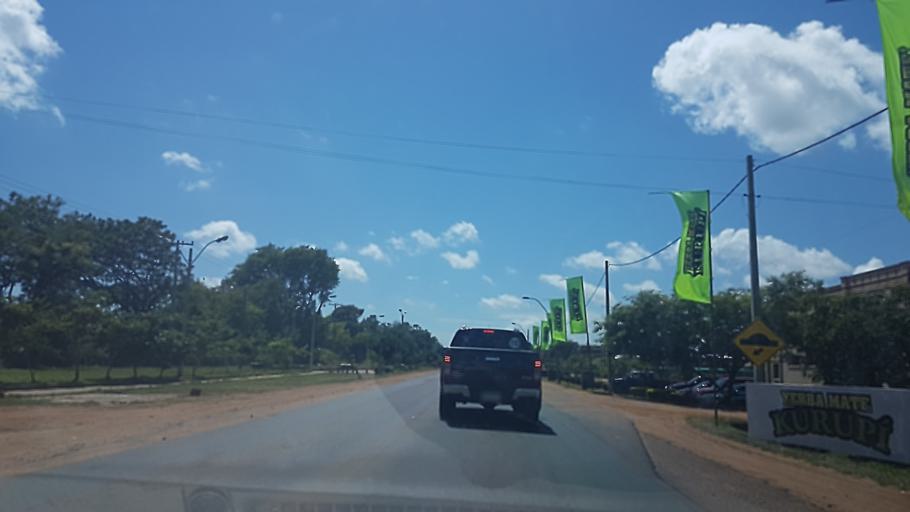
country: PY
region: Misiones
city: San Juan Bautista
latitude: -26.6731
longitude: -57.1194
